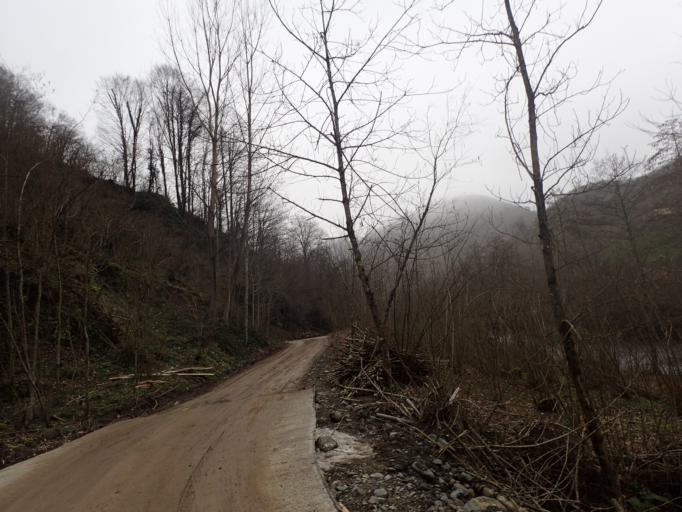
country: TR
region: Ordu
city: Camas
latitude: 40.9170
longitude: 37.5565
